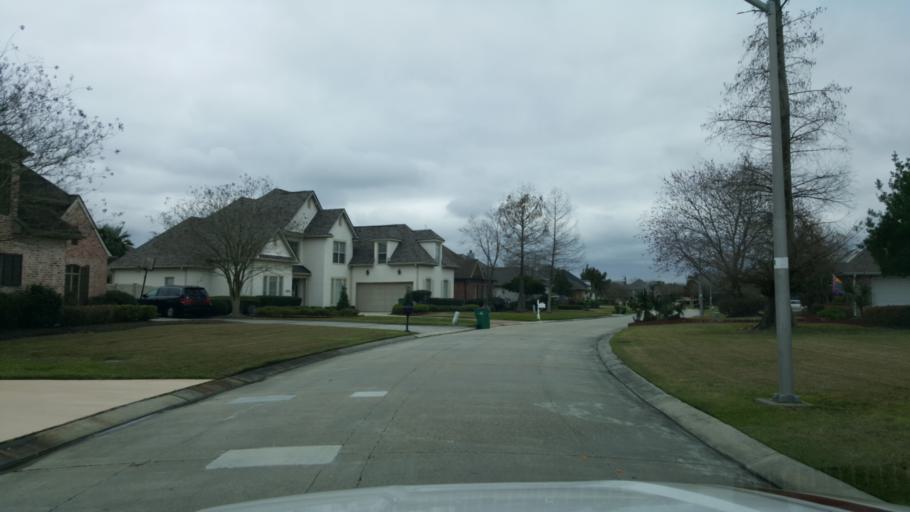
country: US
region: Louisiana
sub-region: Jefferson Parish
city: Woodmere
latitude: 29.8779
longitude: -90.0778
